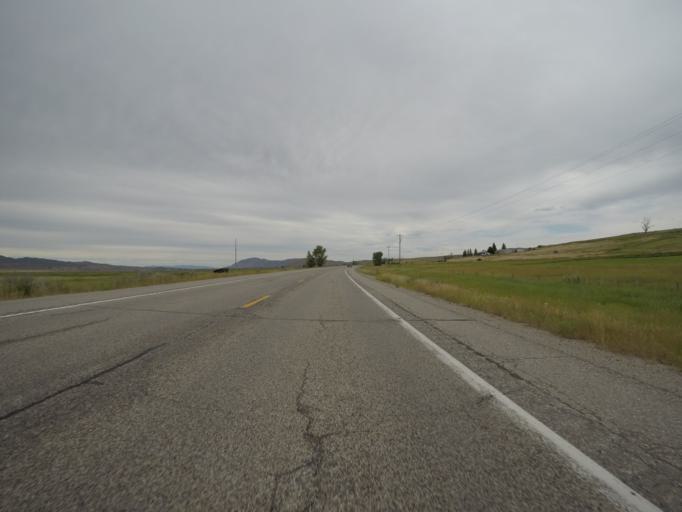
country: US
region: Utah
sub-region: Rich County
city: Randolph
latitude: 42.0333
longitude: -110.9325
